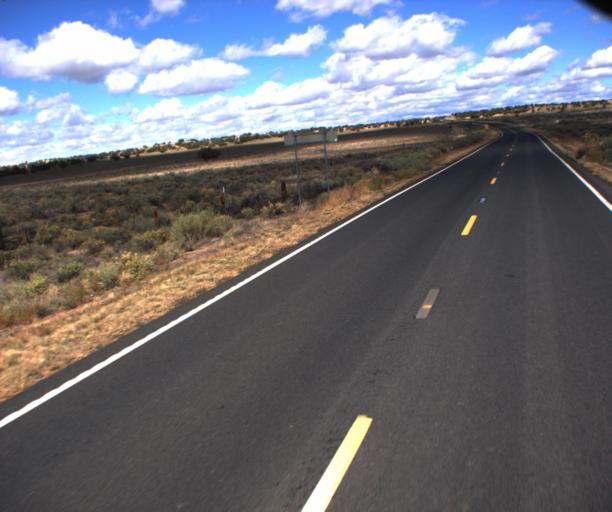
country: US
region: Arizona
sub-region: Apache County
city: Houck
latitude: 35.0949
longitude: -109.3121
